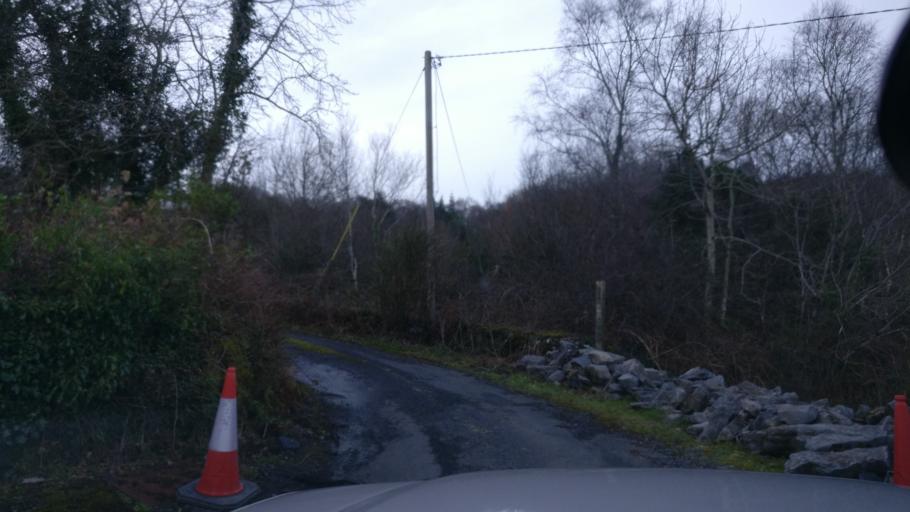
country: IE
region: Connaught
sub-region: County Galway
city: Oughterard
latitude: 53.5191
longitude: -9.4398
